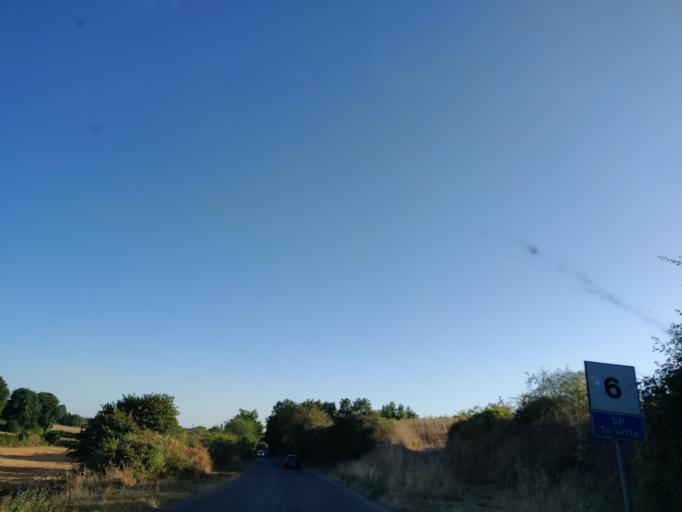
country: IT
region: Latium
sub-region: Provincia di Viterbo
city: Grotte di Castro
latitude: 42.6895
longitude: 11.8756
